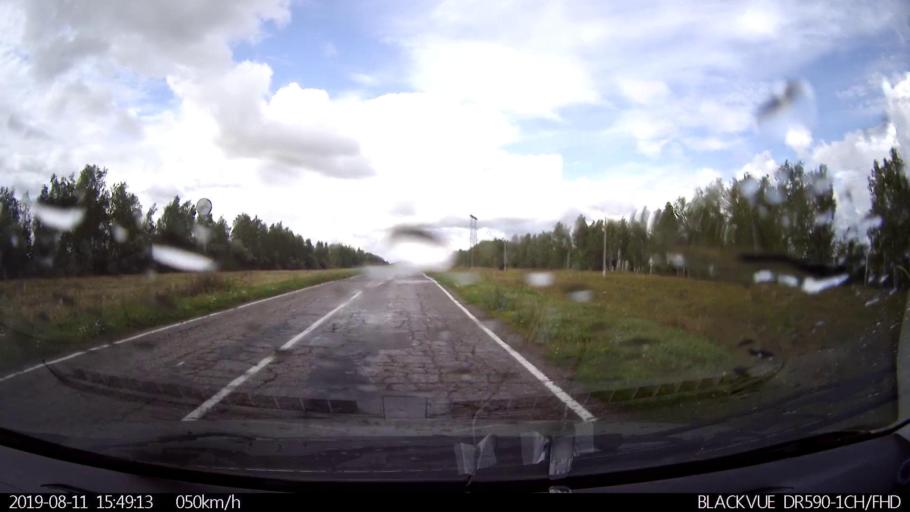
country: RU
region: Ulyanovsk
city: Ignatovka
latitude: 53.9026
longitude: 47.6548
